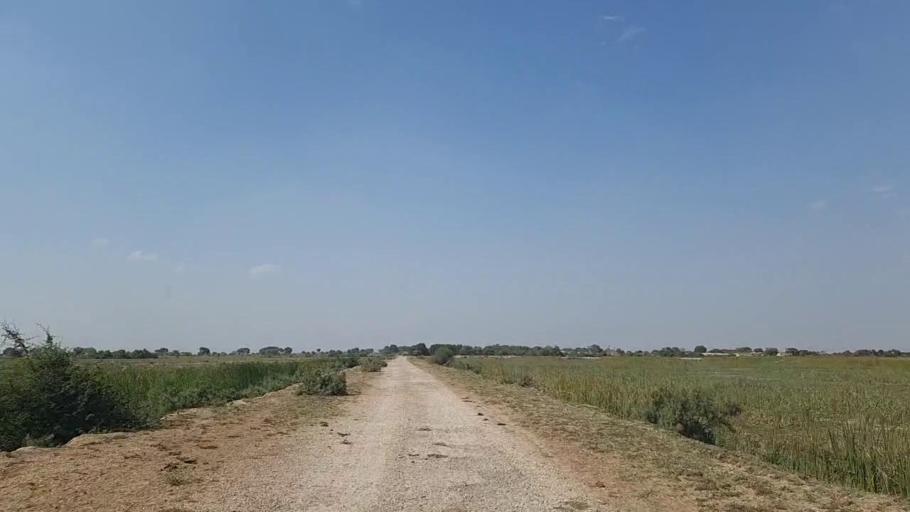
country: PK
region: Sindh
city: Jati
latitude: 24.5149
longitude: 68.2946
